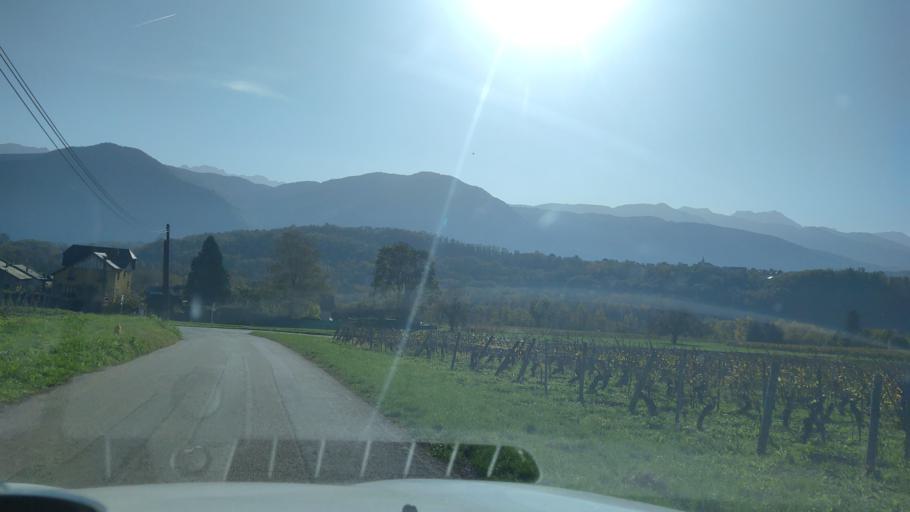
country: FR
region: Rhone-Alpes
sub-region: Departement de la Savoie
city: Coise-Saint-Jean-Pied-Gauthier
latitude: 45.5626
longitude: 6.1681
